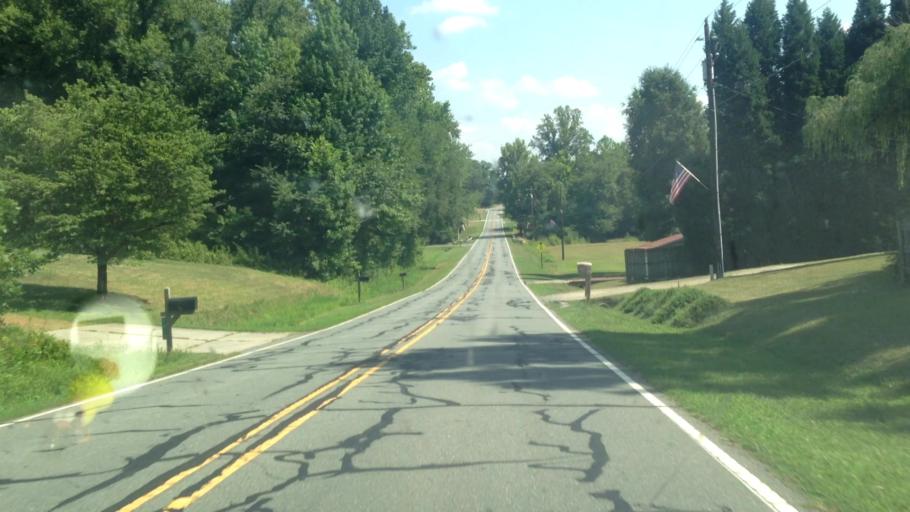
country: US
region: North Carolina
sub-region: Stokes County
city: Walnut Cove
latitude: 36.3351
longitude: -80.0494
